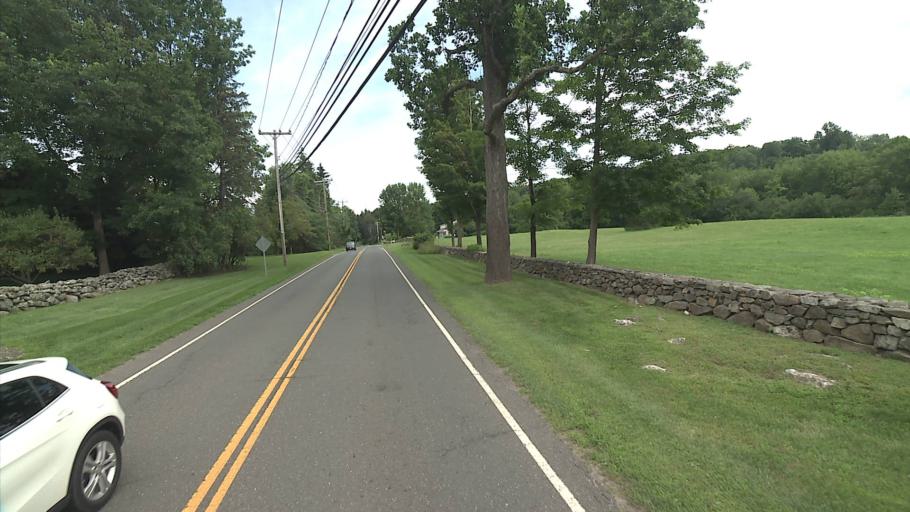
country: US
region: Connecticut
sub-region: Litchfield County
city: New Milford
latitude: 41.5591
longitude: -73.3098
